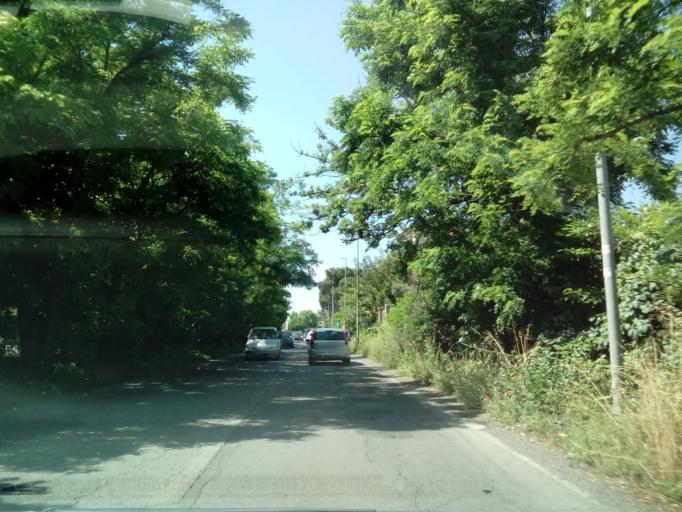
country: IT
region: Latium
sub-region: Citta metropolitana di Roma Capitale
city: Rome
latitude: 41.8773
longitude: 12.5891
